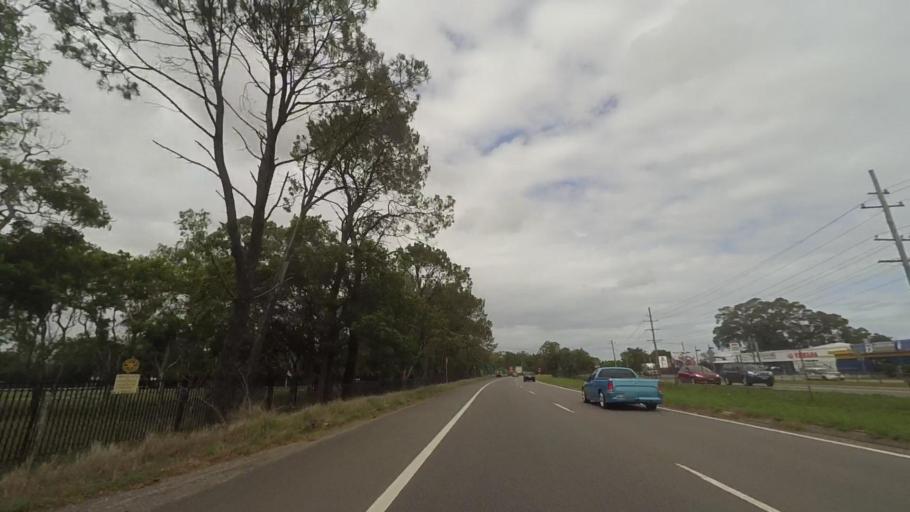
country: AU
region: New South Wales
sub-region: Port Stephens Shire
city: Raymond Terrace
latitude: -32.7836
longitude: 151.7346
